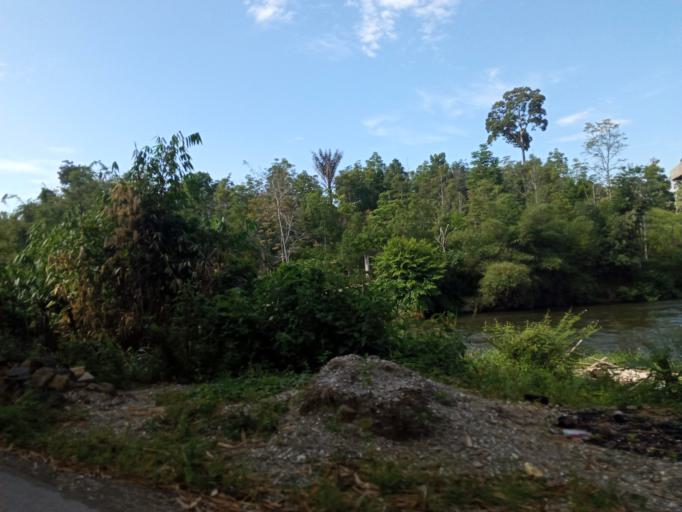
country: ID
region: Jambi
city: Sungai Penuh
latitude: -2.1712
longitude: 101.5987
